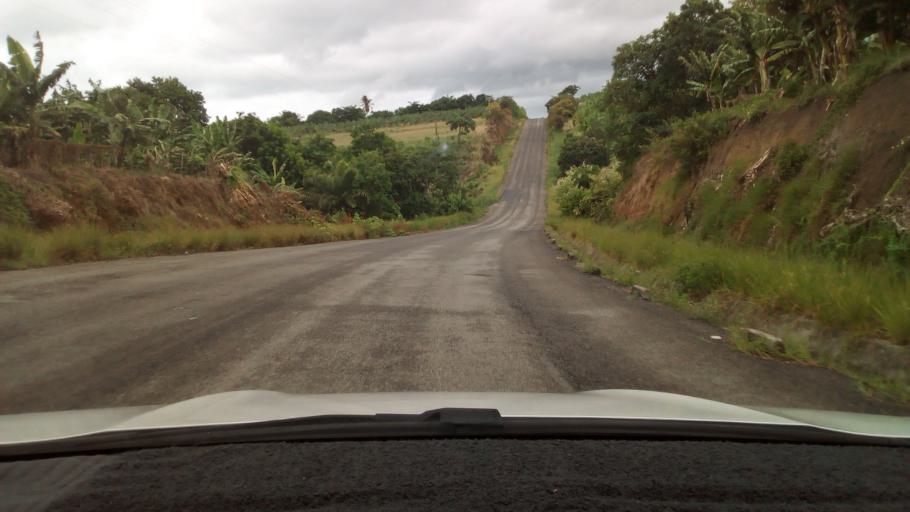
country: BR
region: Paraiba
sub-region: Pitimbu
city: Pitimbu
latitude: -7.3587
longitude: -34.8198
